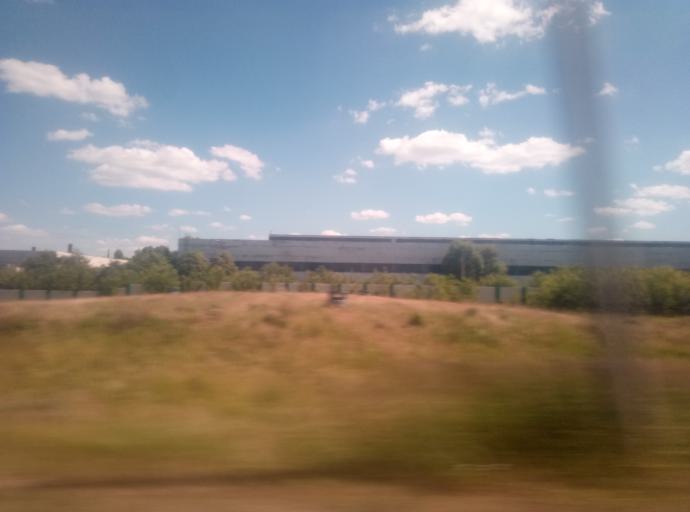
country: RU
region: Tula
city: Kireyevsk
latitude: 53.9589
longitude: 37.9381
